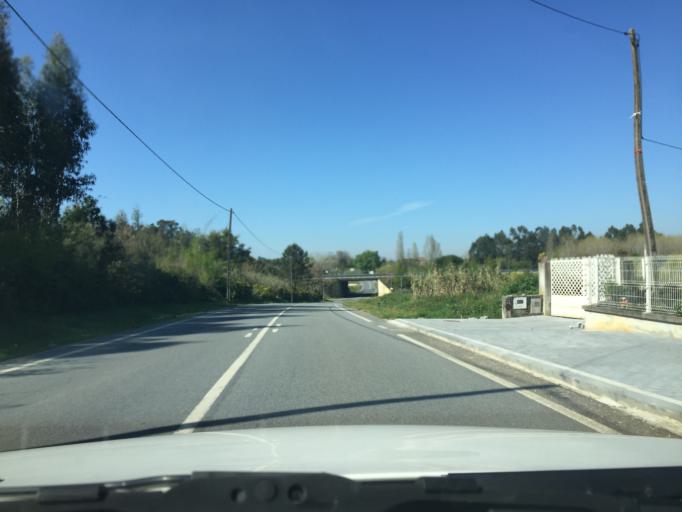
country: PT
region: Aveiro
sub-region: Anadia
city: Sangalhos
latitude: 40.4354
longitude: -8.5055
